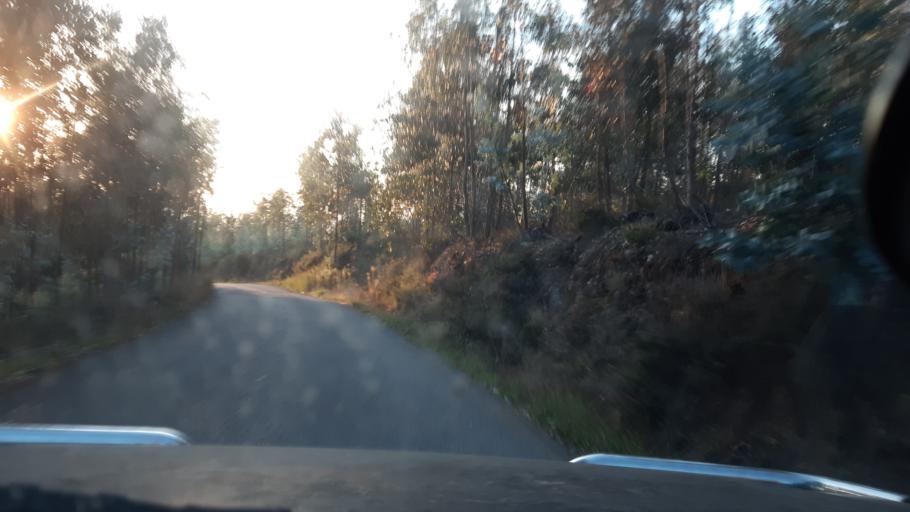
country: PT
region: Aveiro
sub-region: Agueda
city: Aguada de Cima
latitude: 40.5675
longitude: -8.3211
